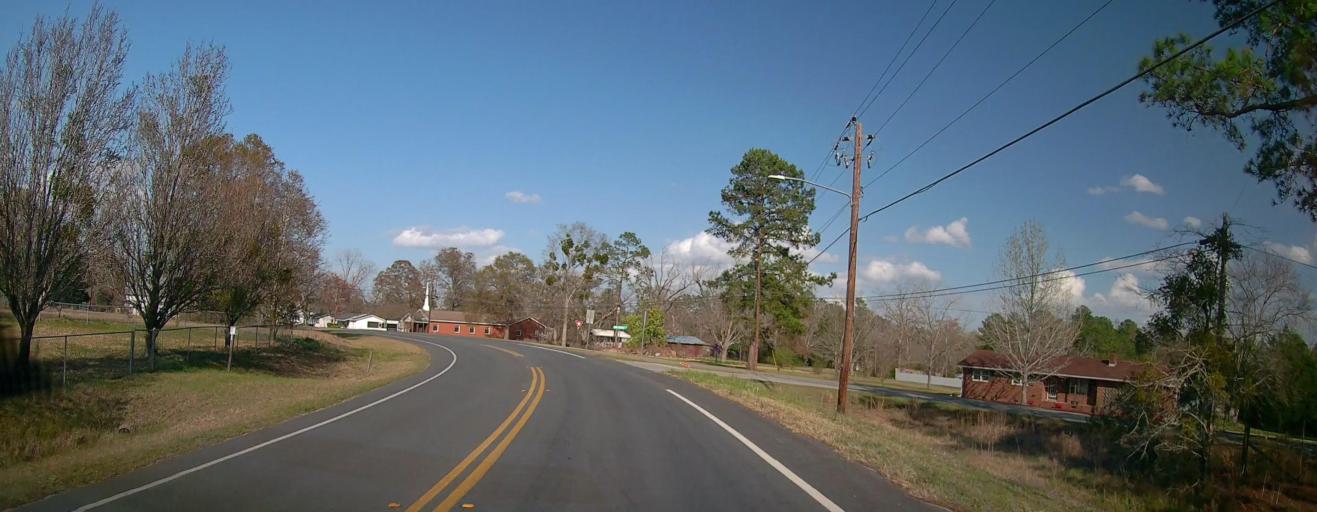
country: US
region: Georgia
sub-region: Telfair County
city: McRae
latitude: 32.0460
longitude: -82.8191
